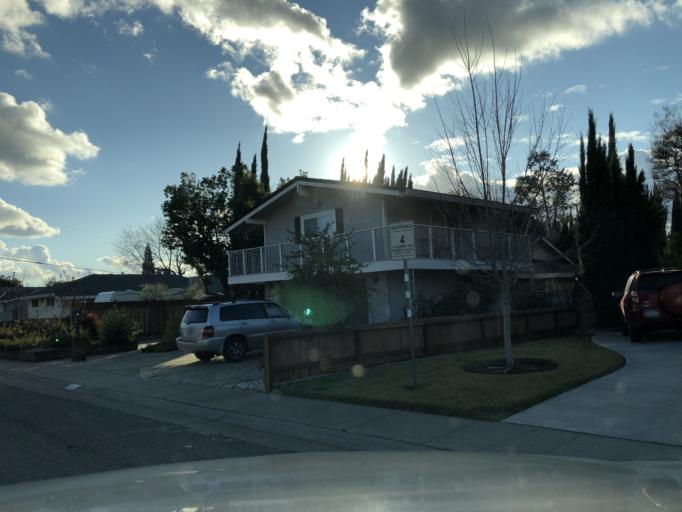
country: US
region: California
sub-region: Sacramento County
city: Fair Oaks
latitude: 38.6621
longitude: -121.3102
